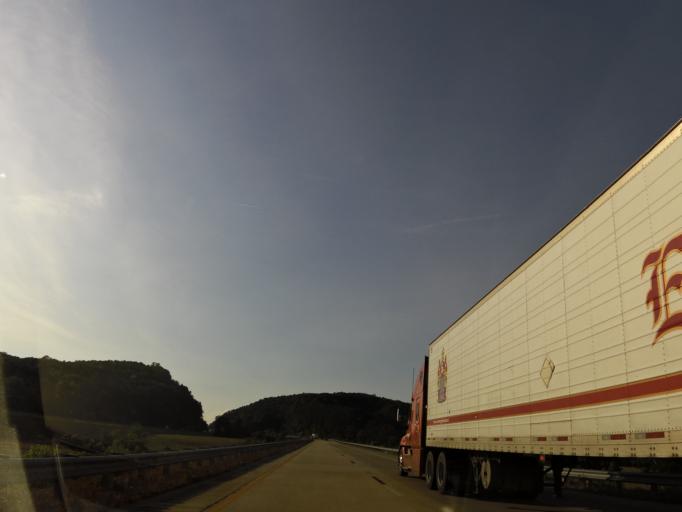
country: US
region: Alabama
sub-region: Etowah County
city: Whitesboro
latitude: 34.1263
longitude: -85.9826
